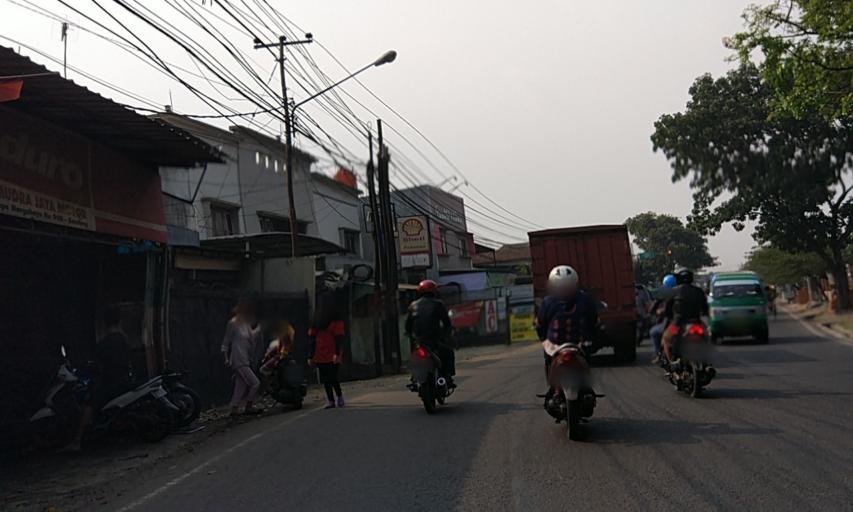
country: ID
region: West Java
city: Margahayukencana
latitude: -6.9776
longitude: 107.5611
